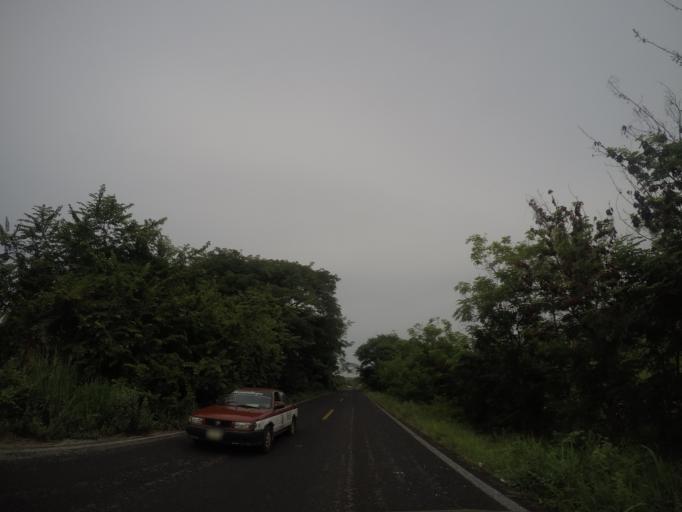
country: MX
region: Oaxaca
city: San Pedro Mixtepec
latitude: 15.9561
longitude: -97.2395
